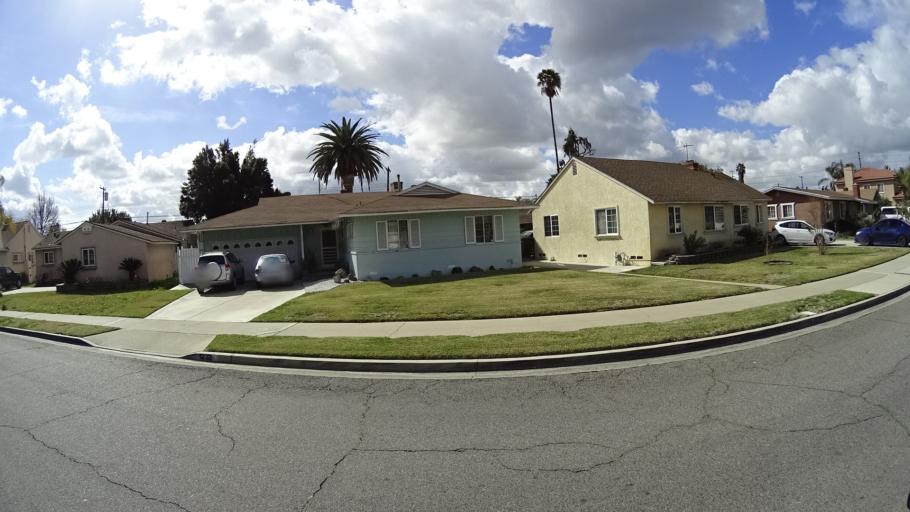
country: US
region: California
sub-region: Orange County
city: Anaheim
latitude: 33.8454
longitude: -117.9035
